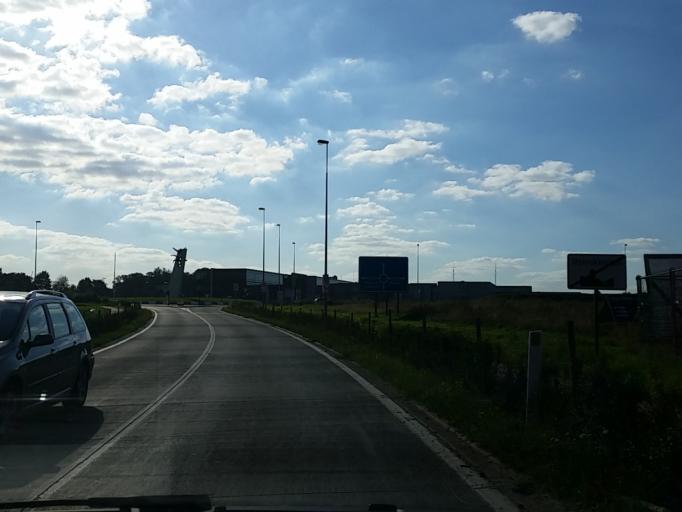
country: BE
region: Flanders
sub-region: Provincie Vlaams-Brabant
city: Steenokkerzeel
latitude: 50.9047
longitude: 4.5140
